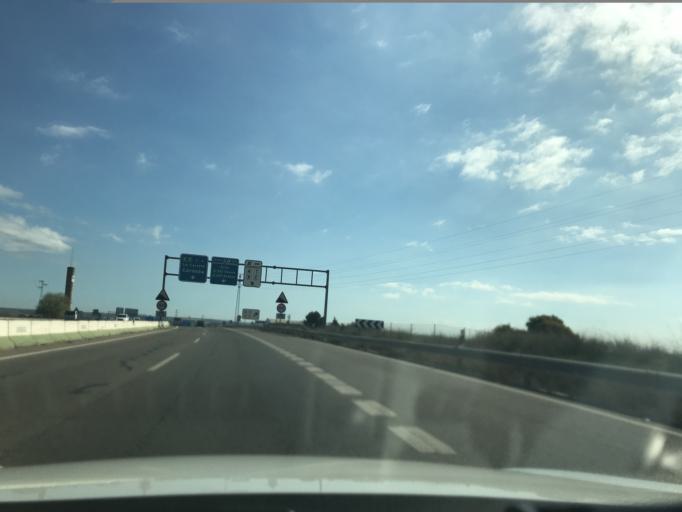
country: ES
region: Andalusia
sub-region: Provincia de Sevilla
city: Ecija
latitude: 37.5263
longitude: -5.1063
